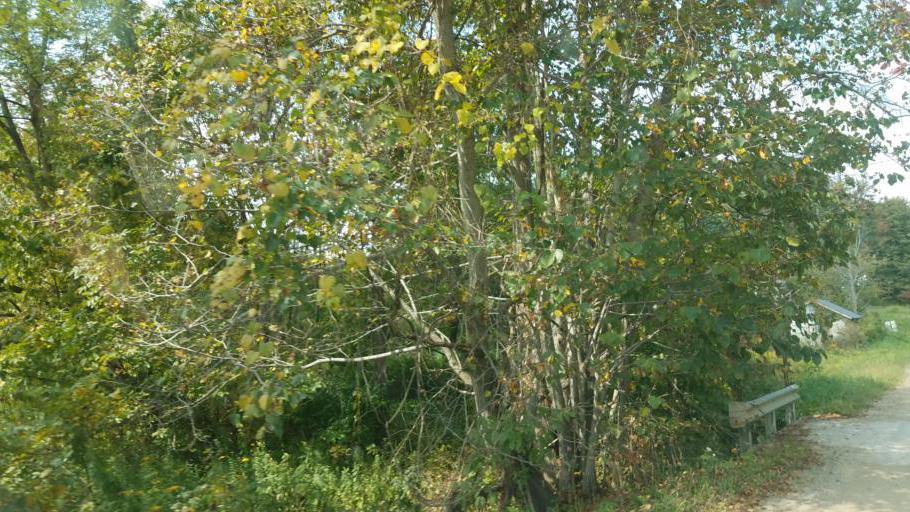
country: US
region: Ohio
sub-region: Knox County
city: Centerburg
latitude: 40.3867
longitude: -82.6314
